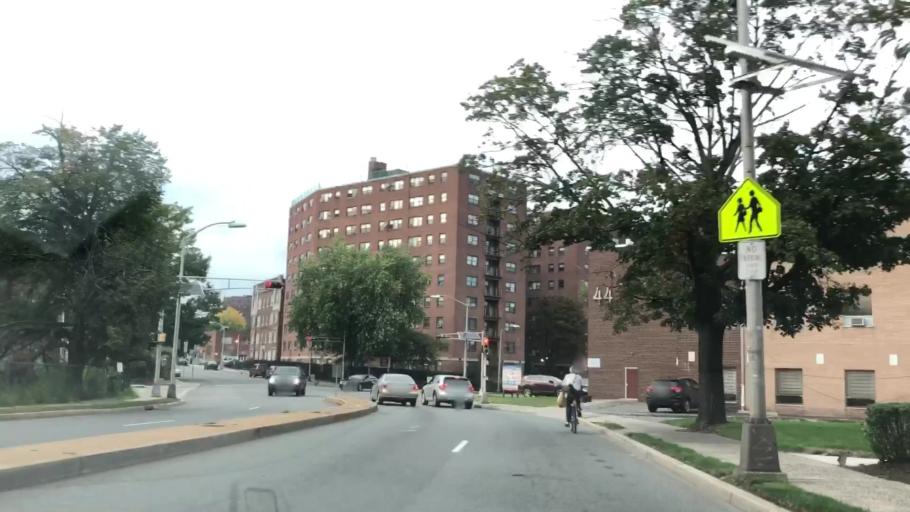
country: US
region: New Jersey
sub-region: Essex County
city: Orange
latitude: 40.7707
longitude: -74.2189
